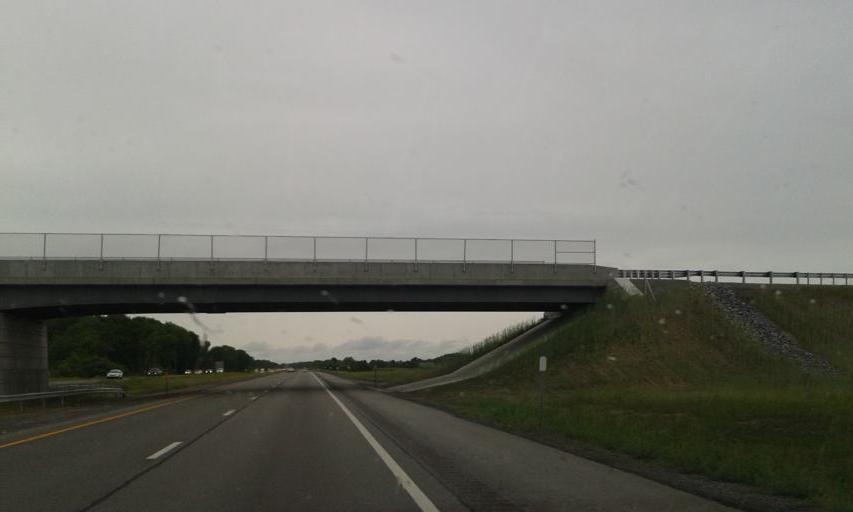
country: US
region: New York
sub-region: Genesee County
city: Le Roy
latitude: 43.0299
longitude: -78.0033
